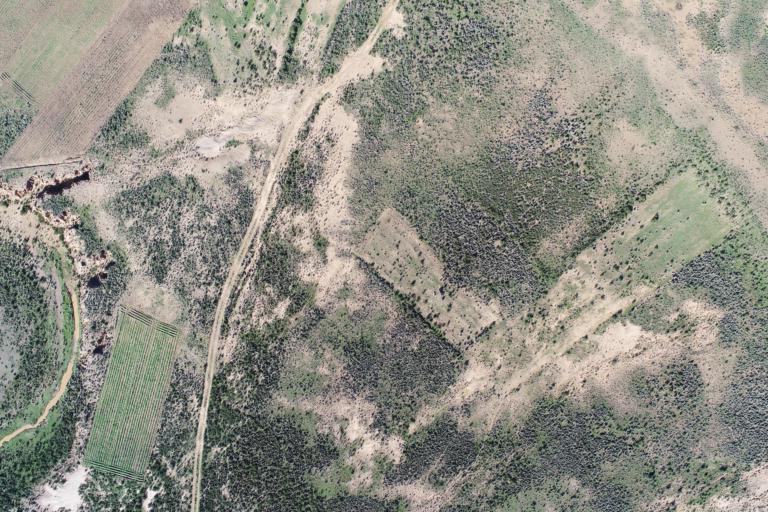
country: BO
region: La Paz
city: Curahuara de Carangas
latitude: -17.3006
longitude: -68.5227
